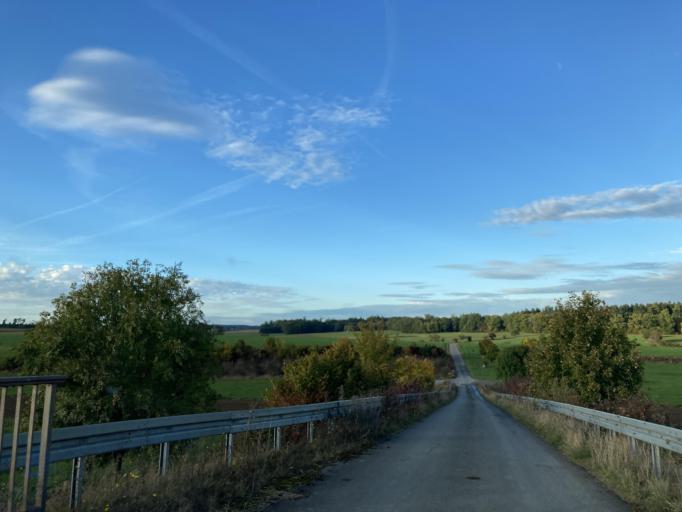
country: DE
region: Baden-Wuerttemberg
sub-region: Regierungsbezirk Stuttgart
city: Motzingen
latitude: 48.5079
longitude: 8.7900
